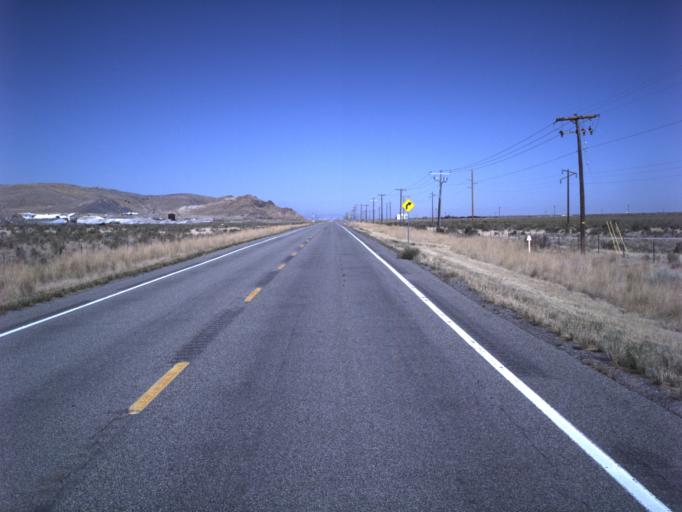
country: US
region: Utah
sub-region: Tooele County
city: Grantsville
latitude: 40.6708
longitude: -112.5469
